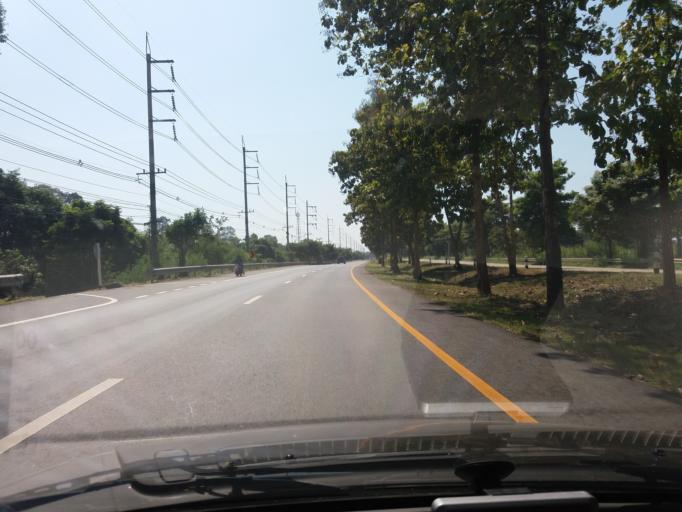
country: TH
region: Chai Nat
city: Sankhaburi
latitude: 15.1138
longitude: 100.1465
